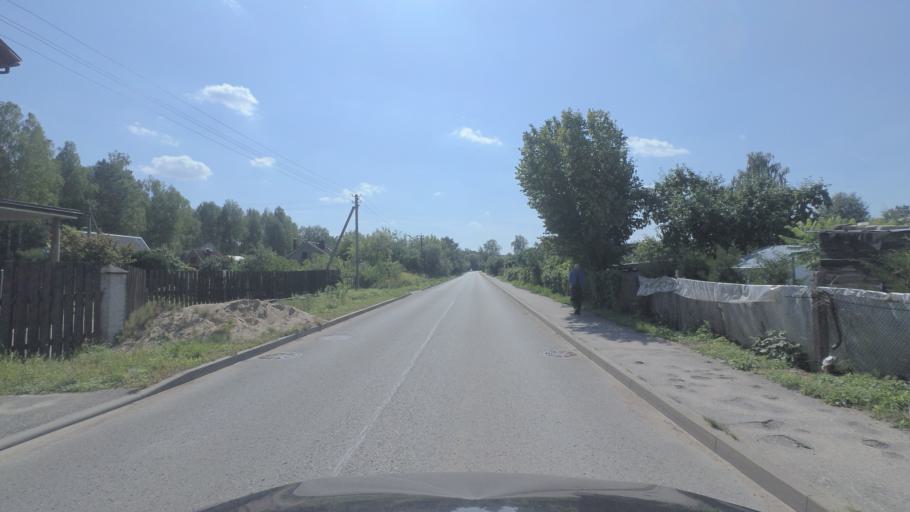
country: LT
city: Nemencine
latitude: 54.8351
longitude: 25.3696
